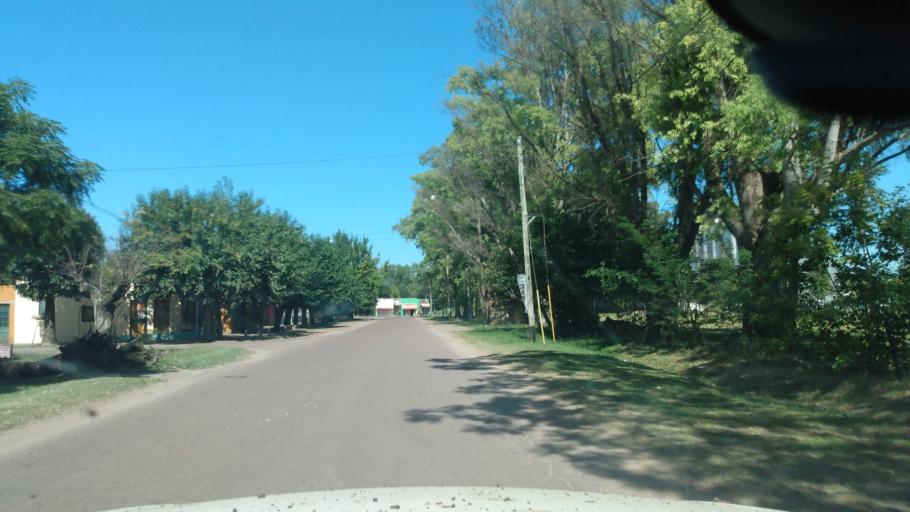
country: AR
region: Buenos Aires
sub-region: Partido de Lujan
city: Lujan
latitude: -34.4890
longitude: -59.0772
